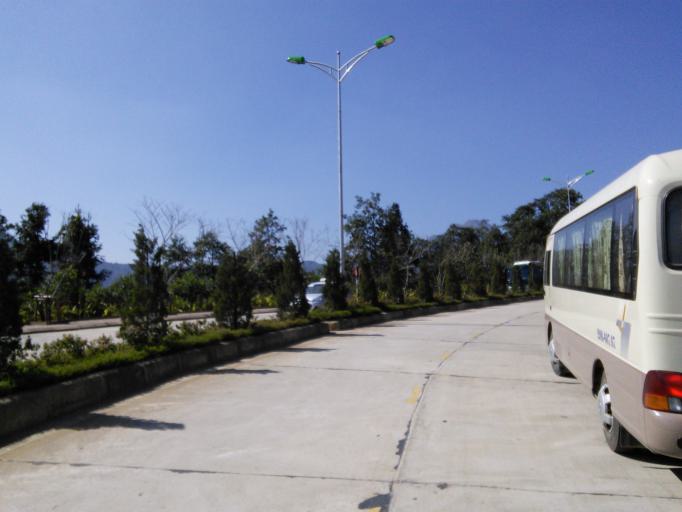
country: VN
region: Lao Cai
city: Sa Pa
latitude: 22.3404
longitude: 103.8245
